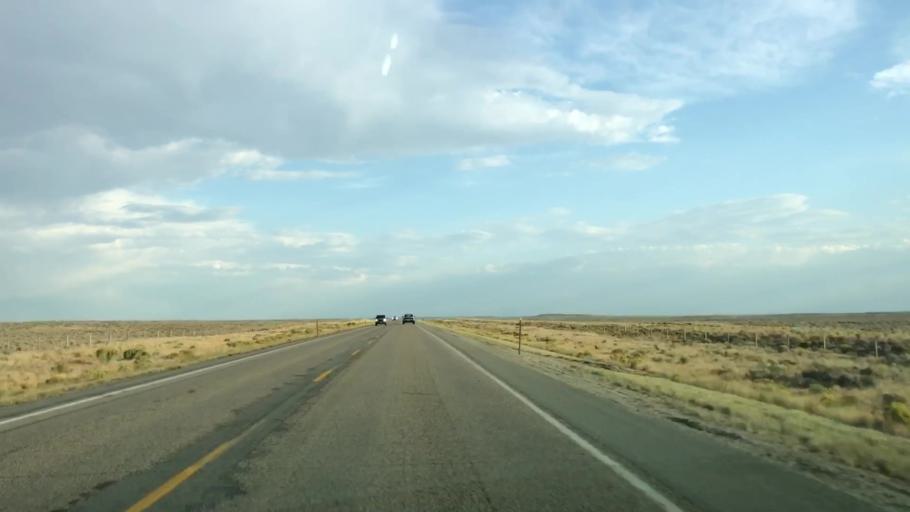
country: US
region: Wyoming
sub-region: Sublette County
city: Pinedale
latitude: 42.4105
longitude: -109.5523
